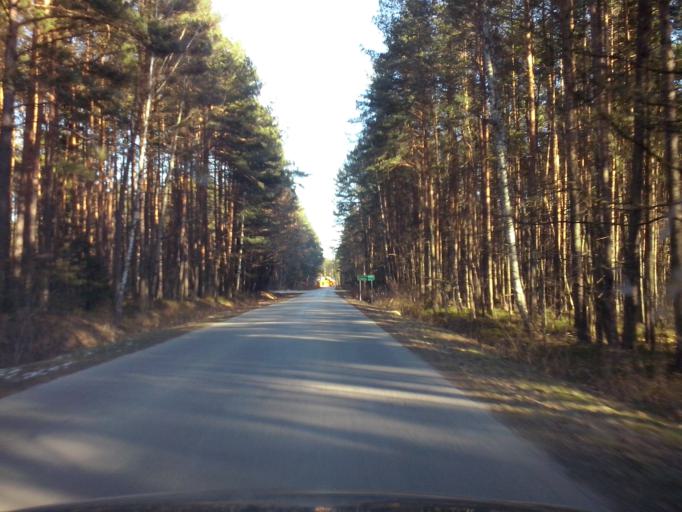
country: PL
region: Subcarpathian Voivodeship
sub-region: Powiat nizanski
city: Harasiuki
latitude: 50.5324
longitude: 22.4458
